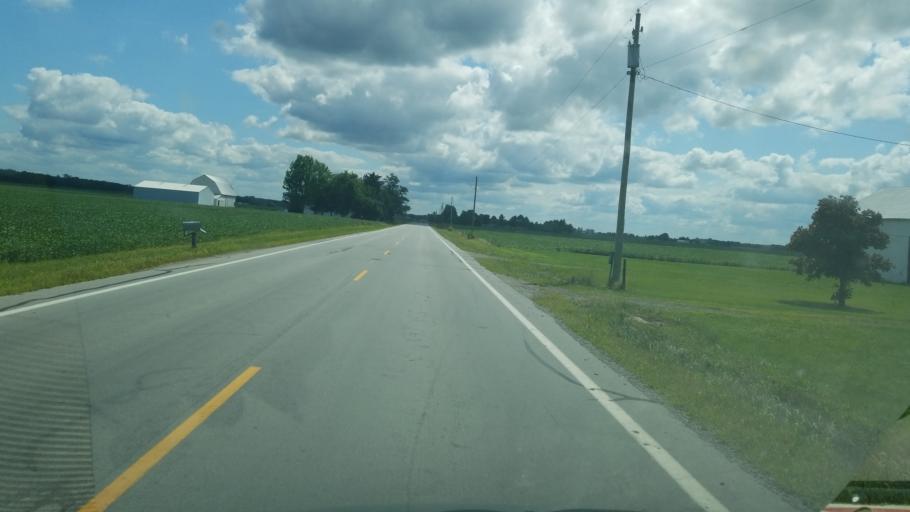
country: US
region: Ohio
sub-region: Allen County
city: Elida
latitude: 40.8517
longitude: -84.1379
